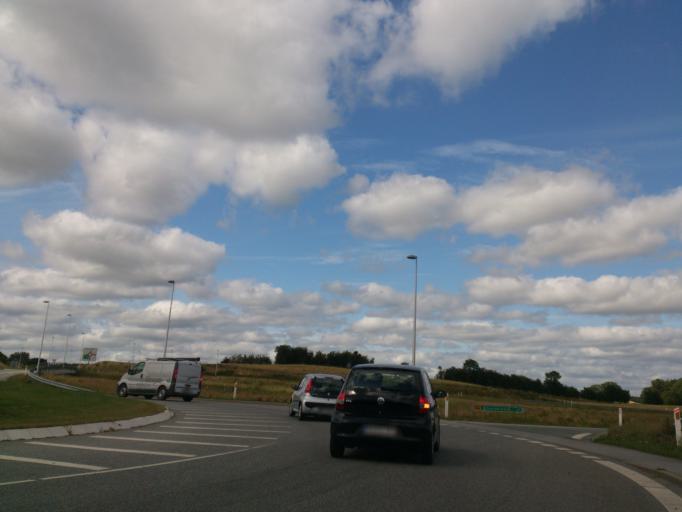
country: DK
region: South Denmark
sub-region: Aabenraa Kommune
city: Krusa
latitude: 54.9439
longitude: 9.4517
